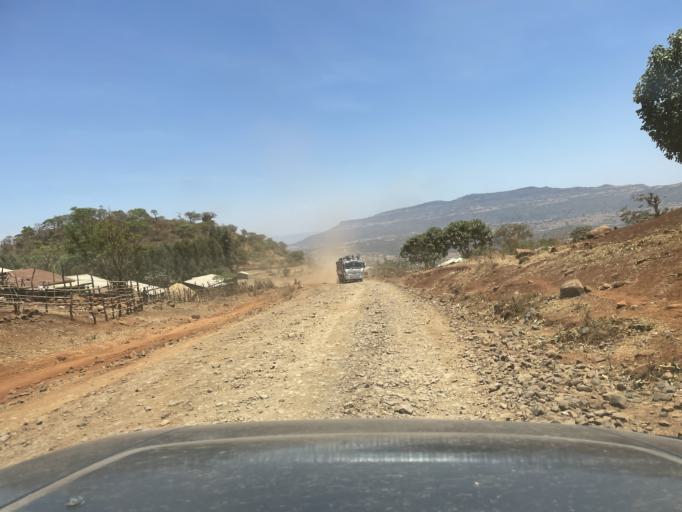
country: ET
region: Amhara
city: Bure
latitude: 10.3846
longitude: 37.0134
